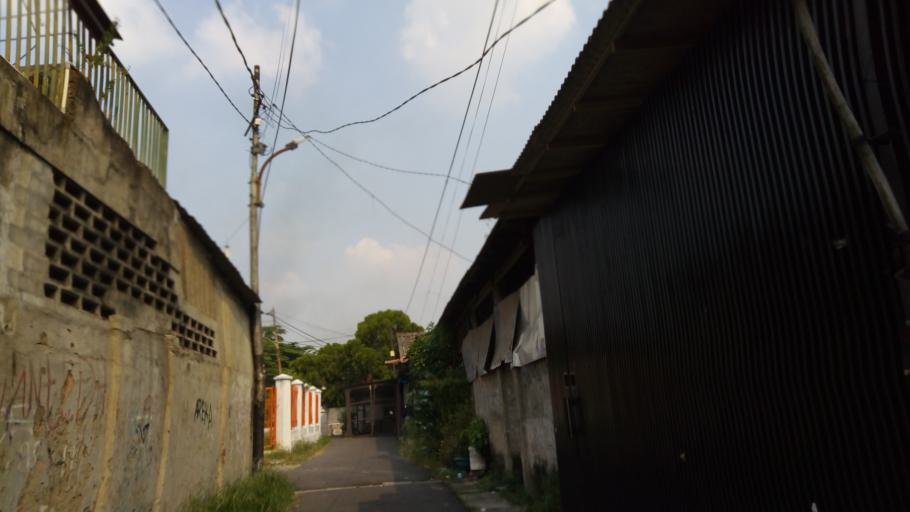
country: ID
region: Jakarta Raya
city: Jakarta
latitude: -6.1785
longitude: 106.8455
